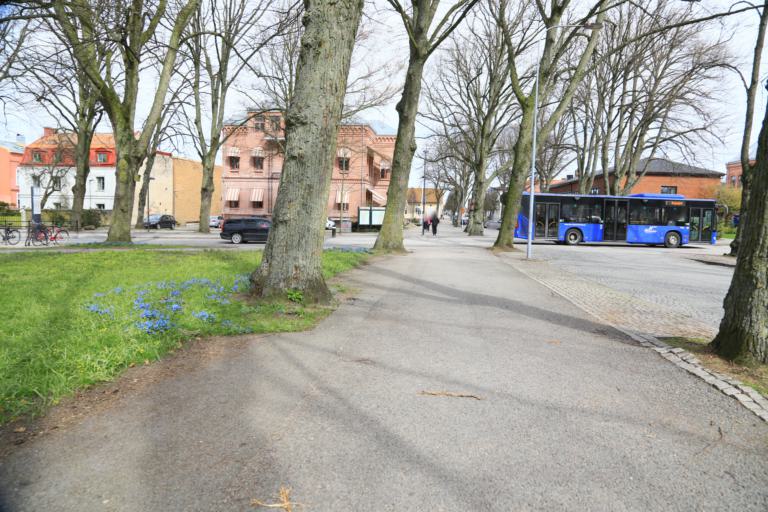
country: SE
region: Halland
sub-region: Varbergs Kommun
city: Varberg
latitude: 57.1079
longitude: 12.2534
